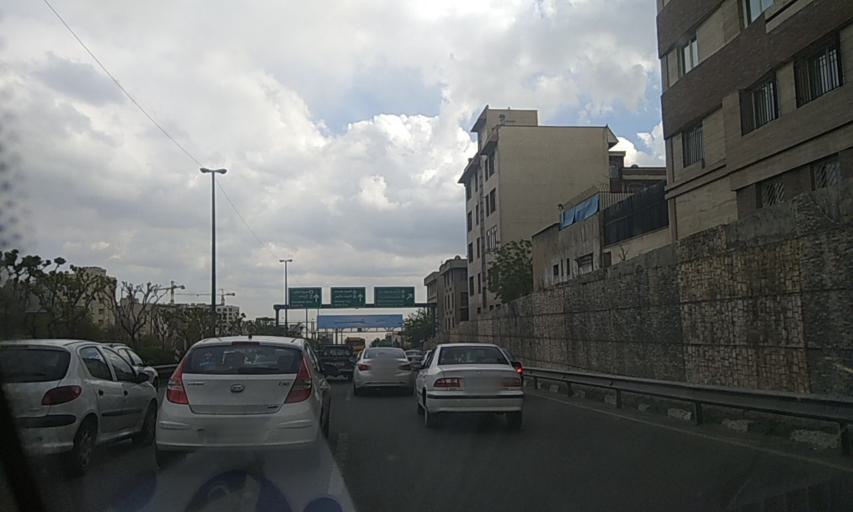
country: IR
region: Tehran
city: Tajrish
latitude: 35.7747
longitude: 51.3444
